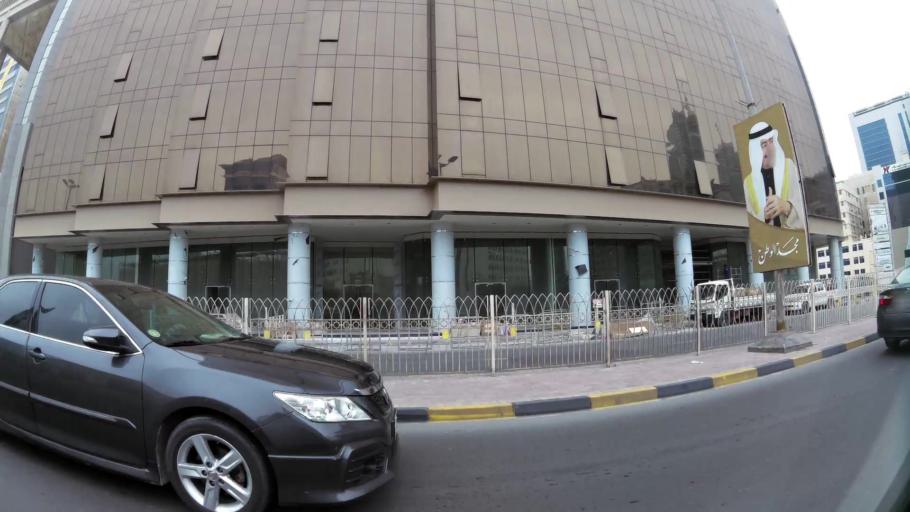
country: BH
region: Manama
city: Manama
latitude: 26.2369
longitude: 50.5793
